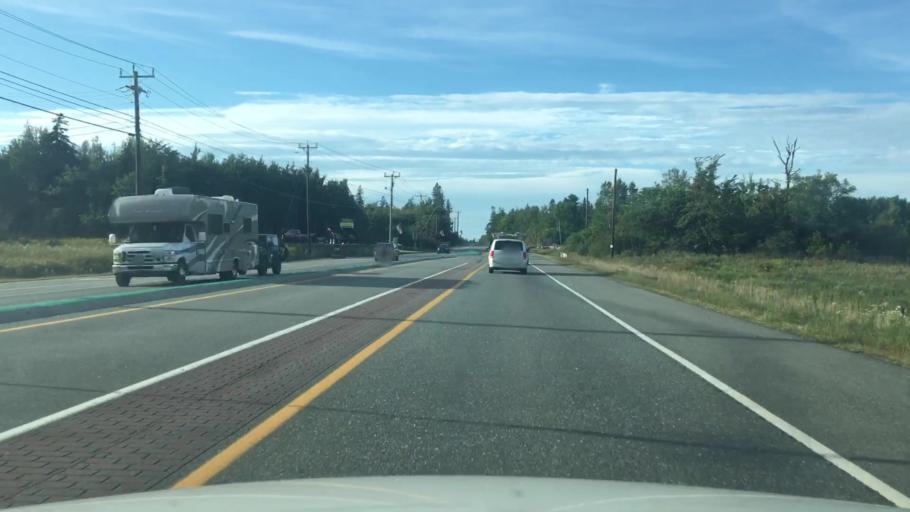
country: US
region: Maine
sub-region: Hancock County
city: Trenton
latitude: 44.4708
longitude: -68.3640
